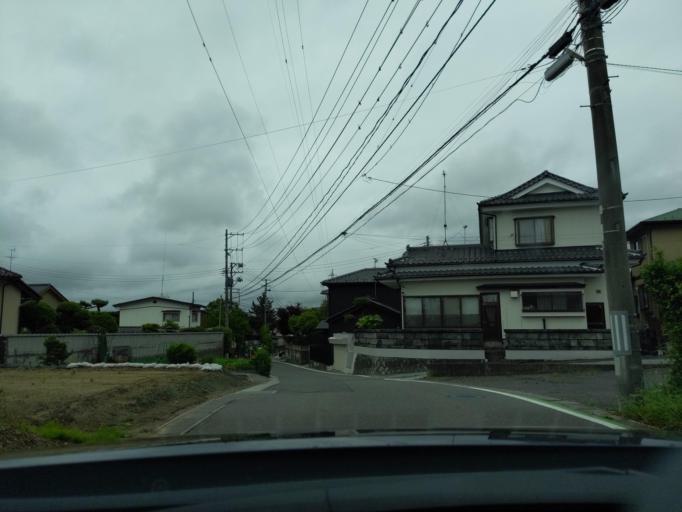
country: JP
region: Fukushima
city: Koriyama
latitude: 37.4202
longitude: 140.3772
